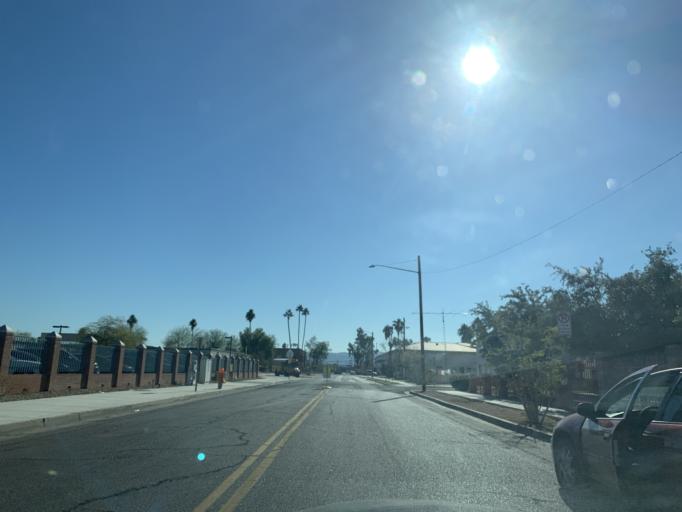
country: US
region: Arizona
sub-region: Maricopa County
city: Phoenix
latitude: 33.4499
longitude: -112.0542
